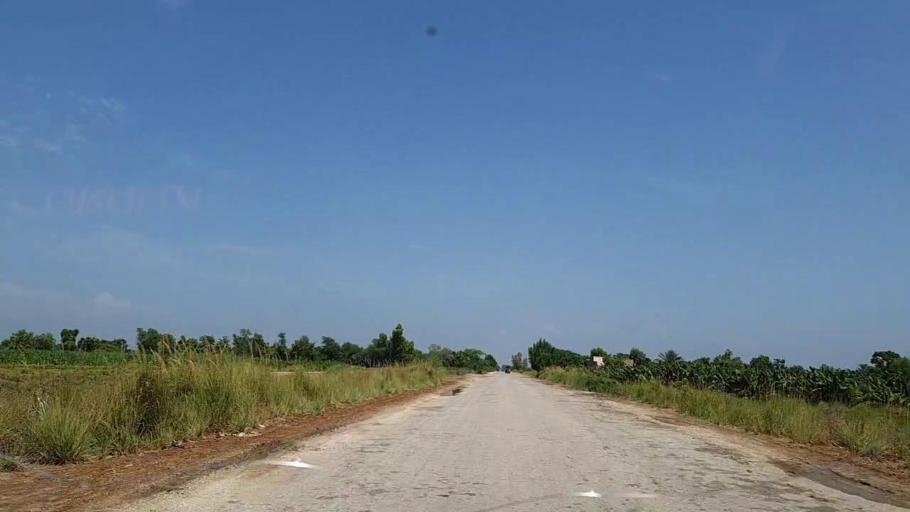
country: PK
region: Sindh
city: Naushahro Firoz
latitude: 26.8209
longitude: 68.1677
